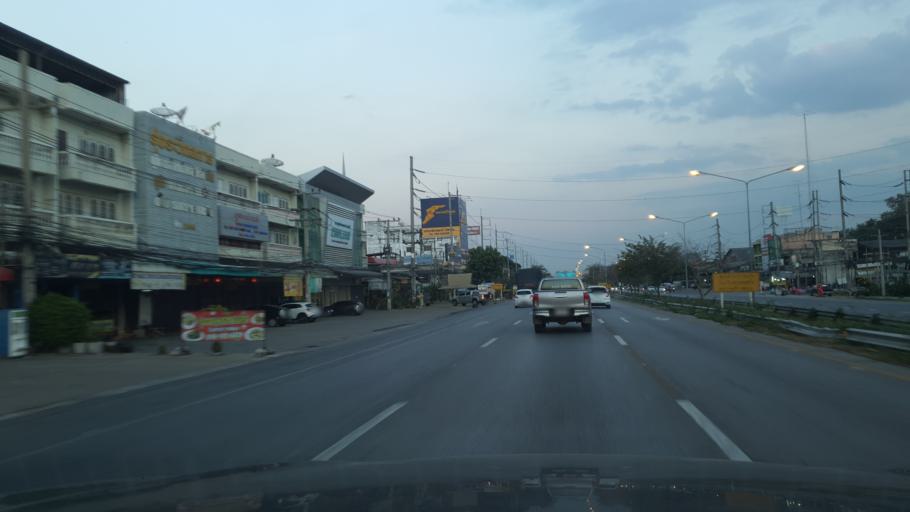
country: TH
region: Nakhon Sawan
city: Nakhon Sawan
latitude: 15.7071
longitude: 100.1013
